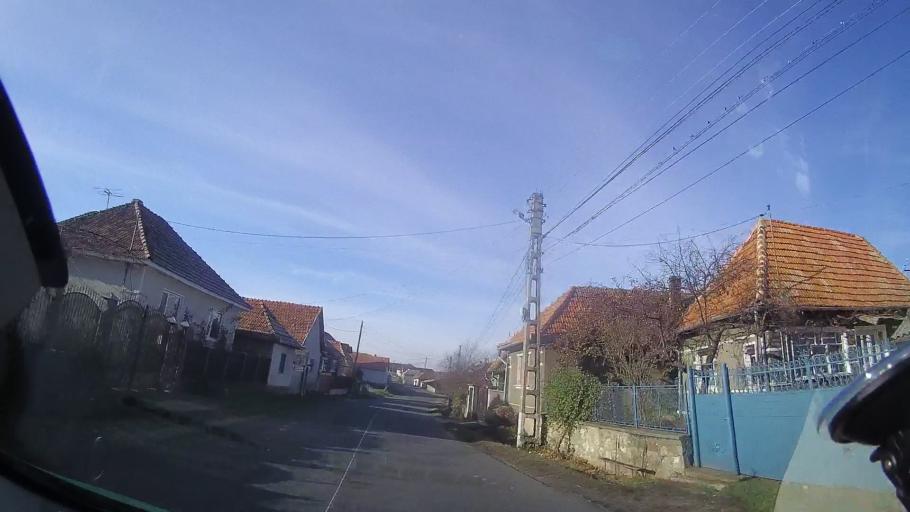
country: RO
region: Bihor
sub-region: Comuna Magesti
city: Magesti
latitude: 47.0176
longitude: 22.4319
